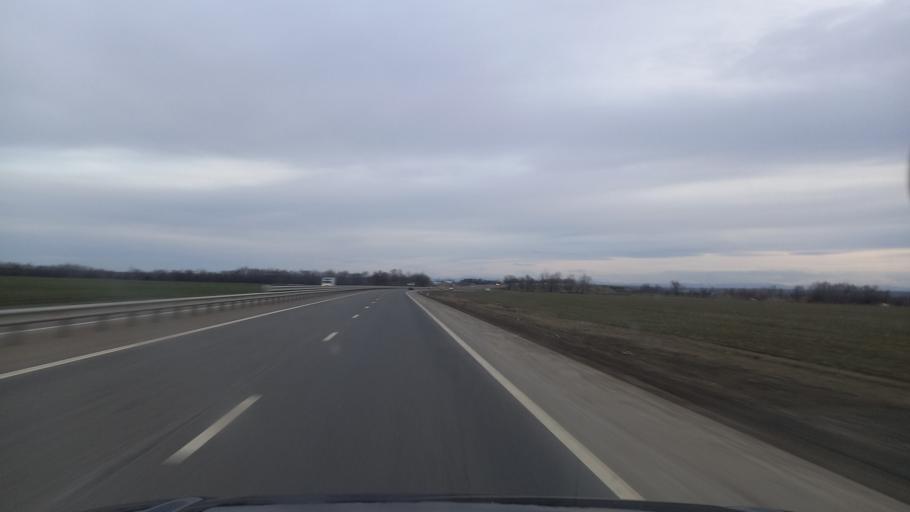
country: RU
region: Adygeya
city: Khanskaya
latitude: 44.7102
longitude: 39.9634
